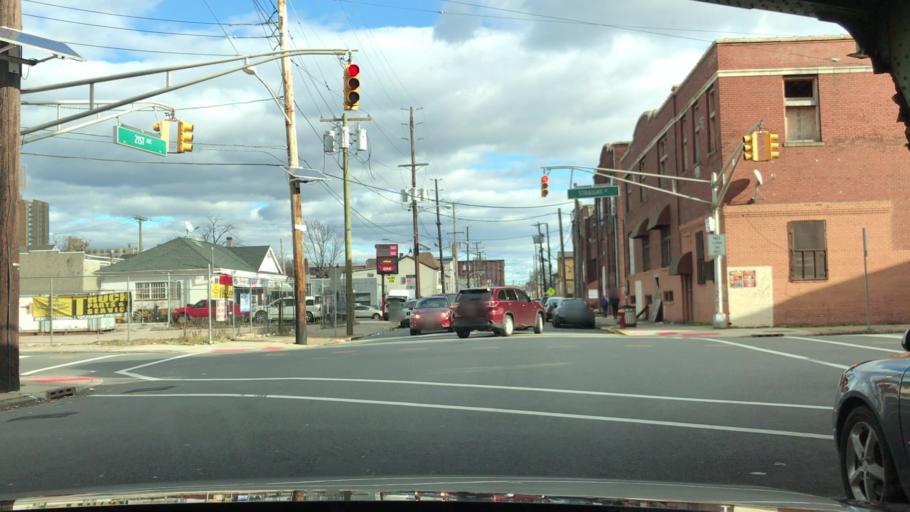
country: US
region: New Jersey
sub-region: Passaic County
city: Paterson
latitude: 40.9078
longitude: -74.1668
